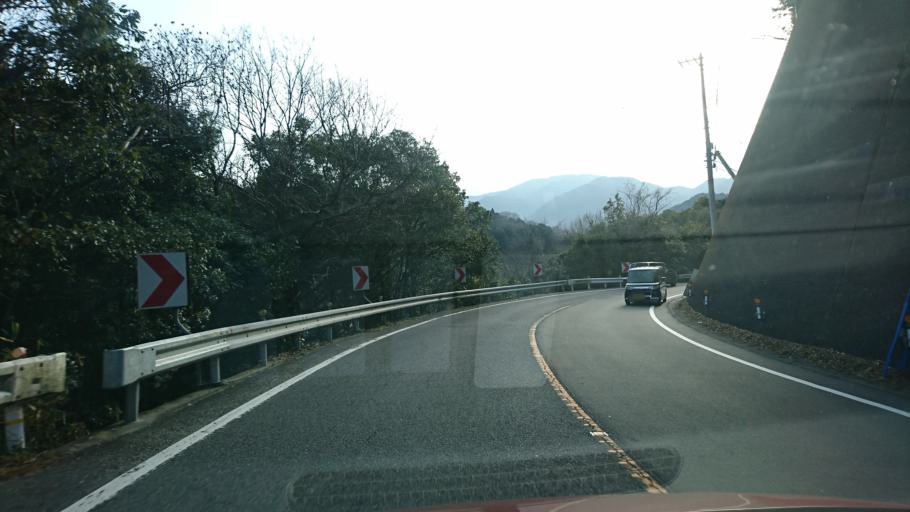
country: JP
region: Ehime
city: Hojo
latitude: 33.9841
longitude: 132.9087
